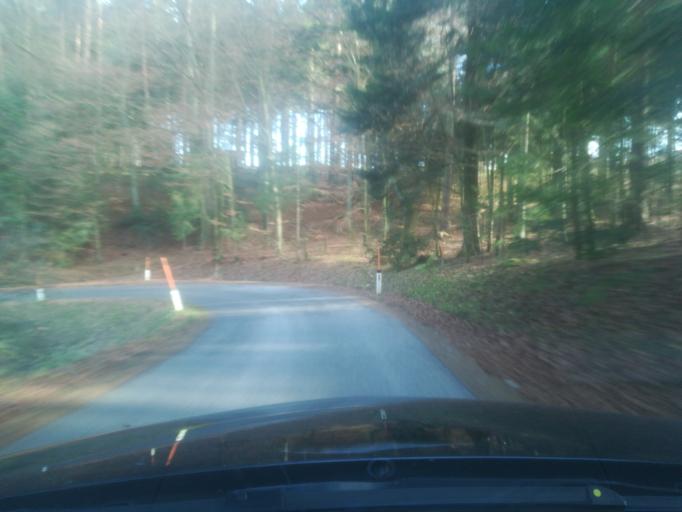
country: AT
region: Upper Austria
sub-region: Politischer Bezirk Perg
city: Perg
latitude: 48.3286
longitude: 14.6517
